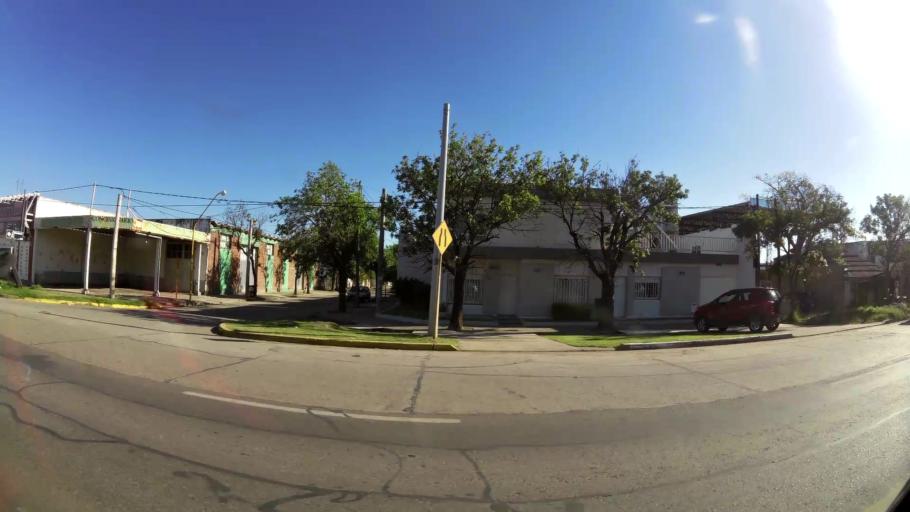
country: AR
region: Cordoba
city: San Francisco
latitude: -31.4153
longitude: -62.0912
